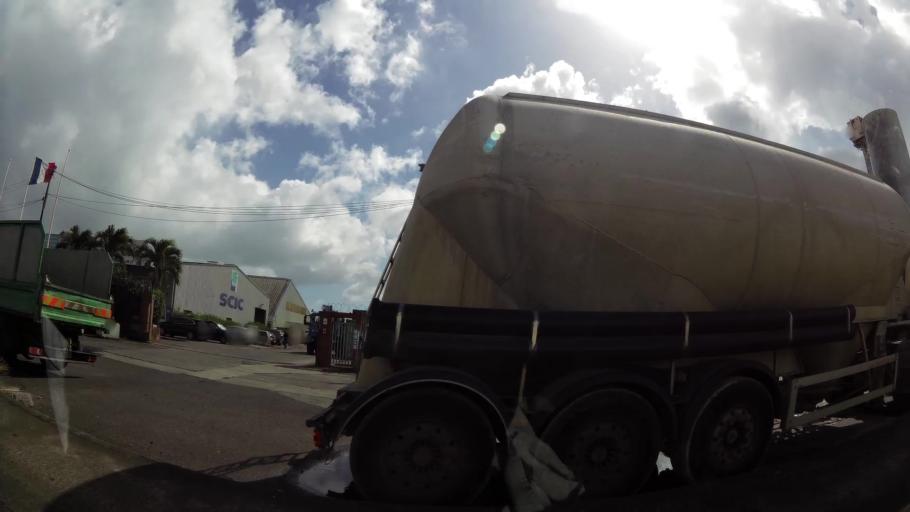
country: MQ
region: Martinique
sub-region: Martinique
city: Fort-de-France
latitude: 14.5961
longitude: -61.0573
